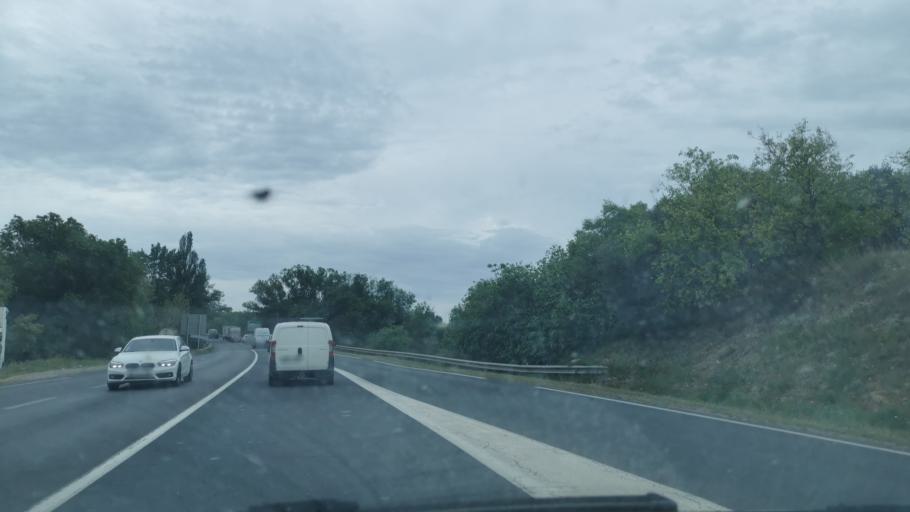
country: FR
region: Languedoc-Roussillon
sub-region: Departement de l'Herault
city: Balaruc-le-Vieux
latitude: 43.4714
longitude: 3.6878
